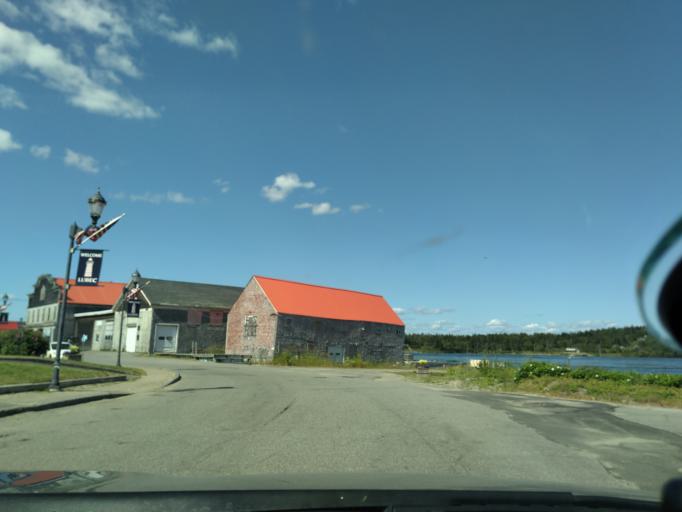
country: US
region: Maine
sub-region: Washington County
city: Eastport
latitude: 44.8592
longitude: -66.9830
